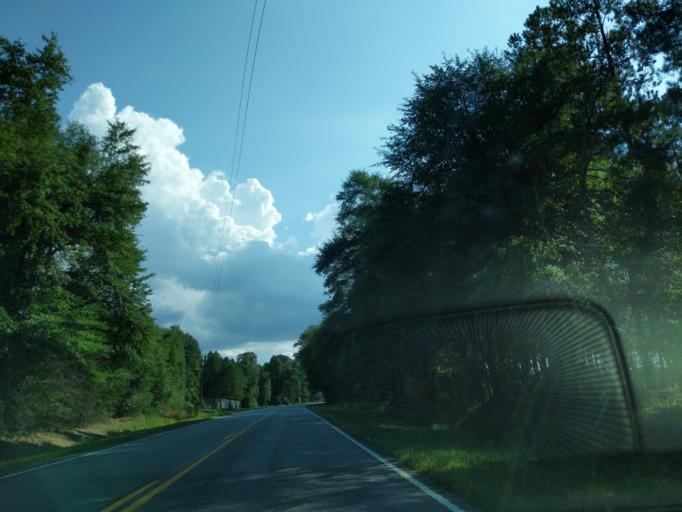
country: US
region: South Carolina
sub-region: Barnwell County
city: Williston
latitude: 33.4378
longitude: -81.3793
